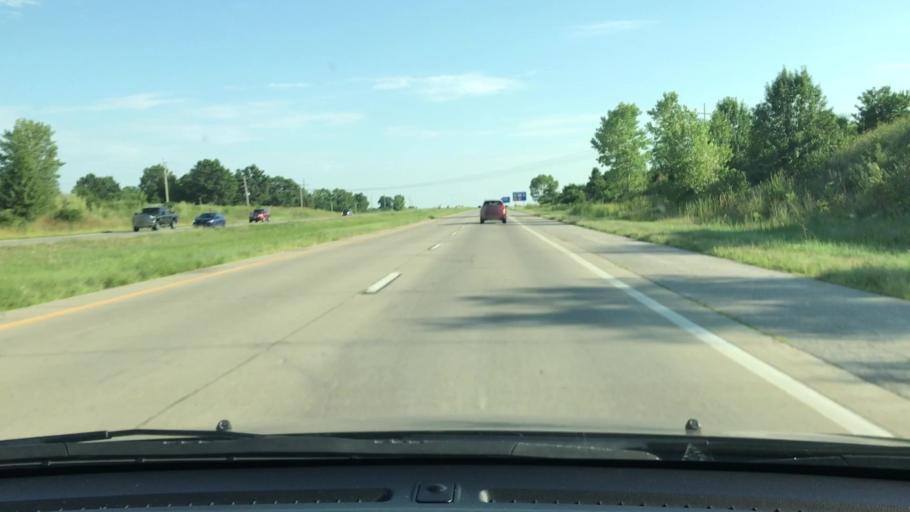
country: US
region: Missouri
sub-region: Jackson County
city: Greenwood
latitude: 38.8649
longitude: -94.3753
